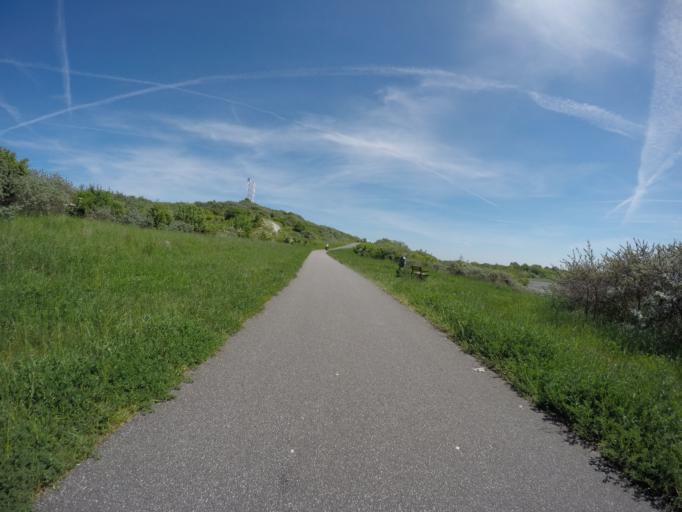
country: SE
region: Skane
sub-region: Malmo
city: Bunkeflostrand
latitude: 55.5632
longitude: 12.9005
